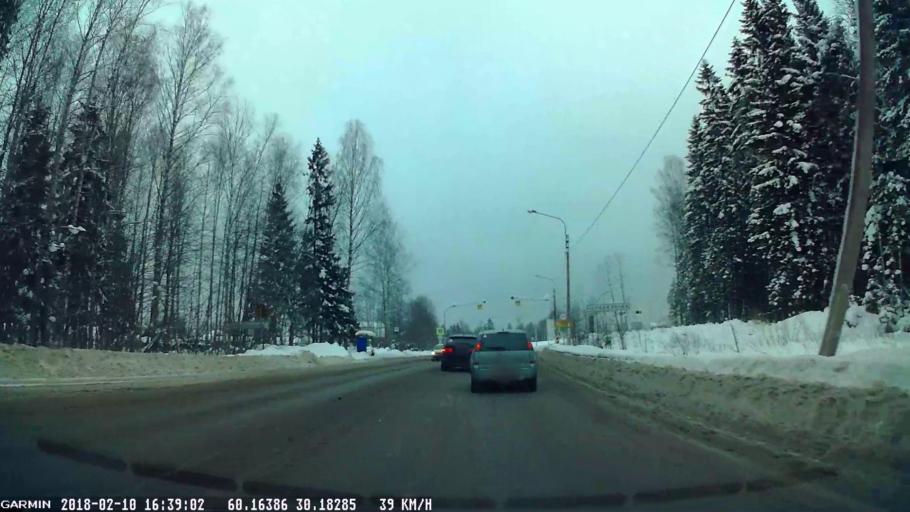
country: RU
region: Leningrad
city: Sertolovo
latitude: 60.1560
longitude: 30.1893
